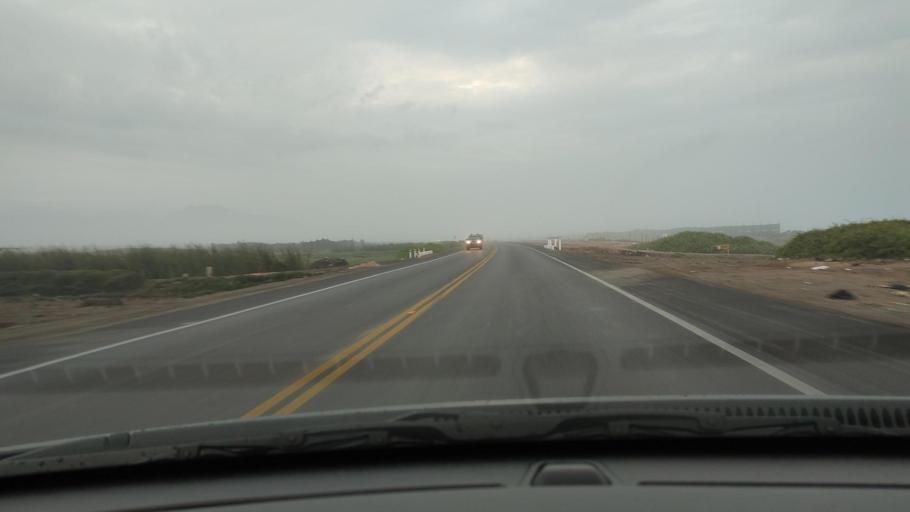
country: PE
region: La Libertad
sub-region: Provincia de Trujillo
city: Huanchaco
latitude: -8.1121
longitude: -79.0943
